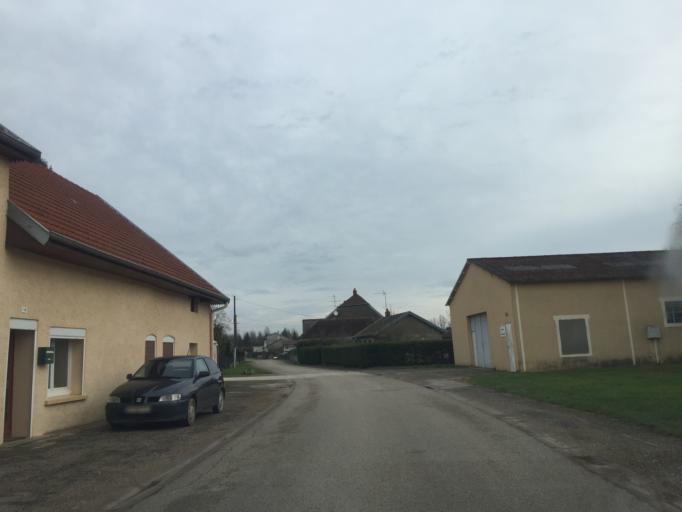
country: FR
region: Franche-Comte
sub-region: Departement du Jura
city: Choisey
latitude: 47.0388
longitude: 5.4461
